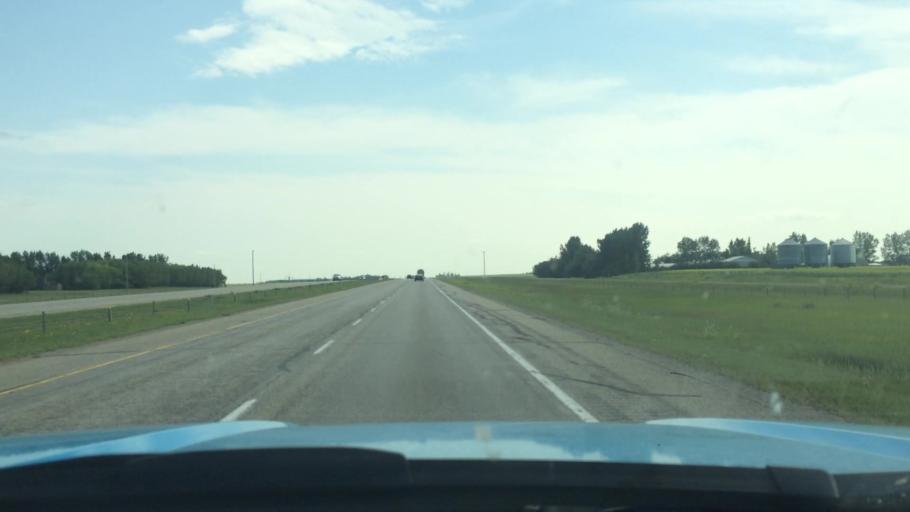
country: CA
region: Alberta
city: Olds
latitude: 51.8349
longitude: -114.0258
